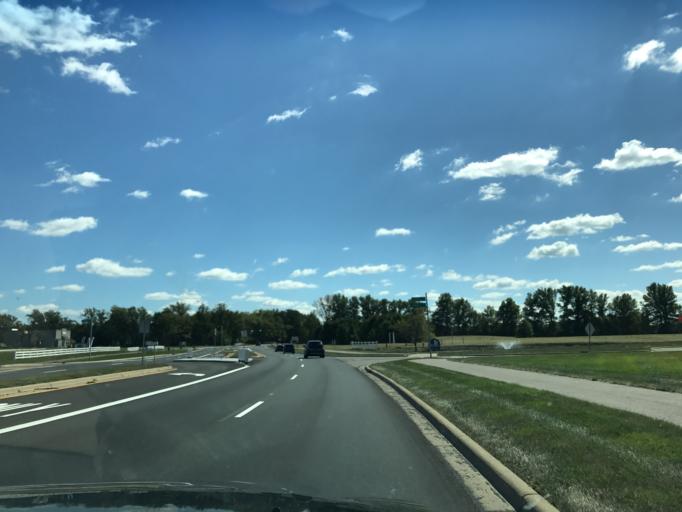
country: US
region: Ohio
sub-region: Delaware County
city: Powell
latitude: 40.1688
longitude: -83.0900
